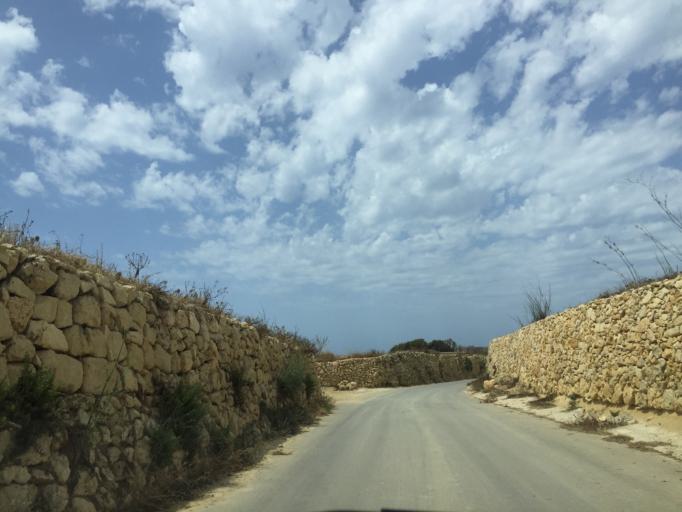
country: MT
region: L-Gharb
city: Gharb
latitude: 36.0695
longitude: 14.2016
